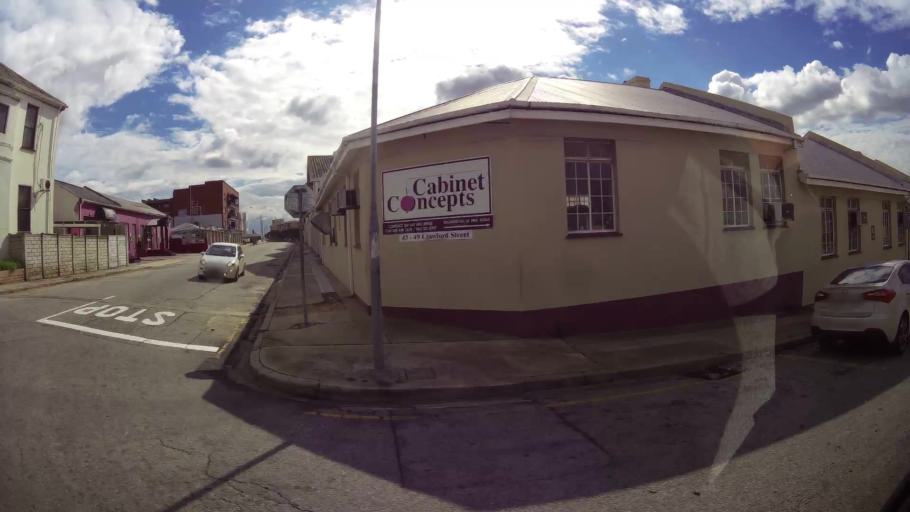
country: ZA
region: Eastern Cape
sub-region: Nelson Mandela Bay Metropolitan Municipality
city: Port Elizabeth
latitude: -33.9484
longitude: 25.6049
